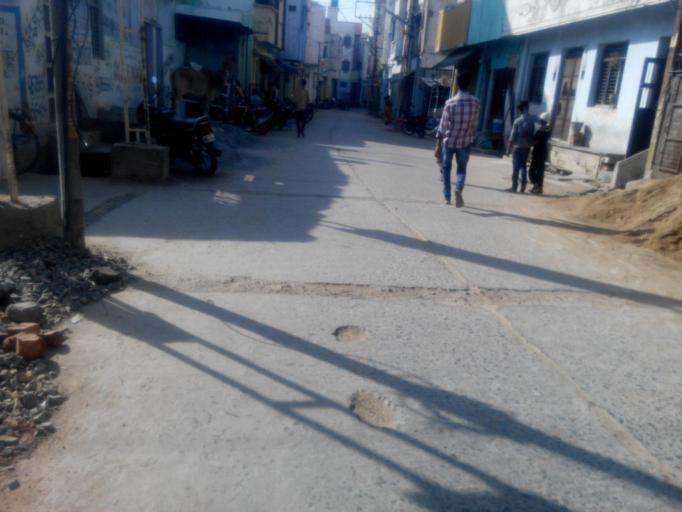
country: IN
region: Andhra Pradesh
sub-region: Kurnool
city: Nandyal
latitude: 15.4907
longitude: 78.4836
